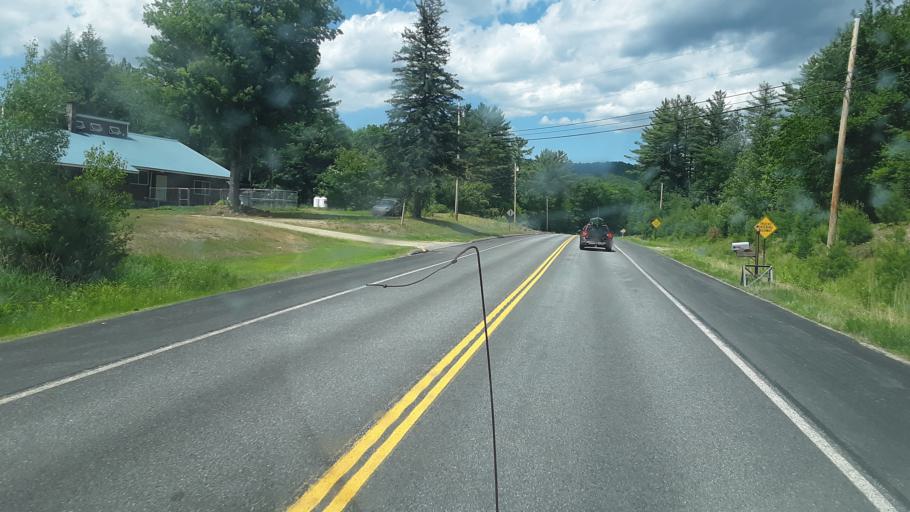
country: US
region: Maine
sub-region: Oxford County
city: Peru
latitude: 44.5382
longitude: -70.4050
